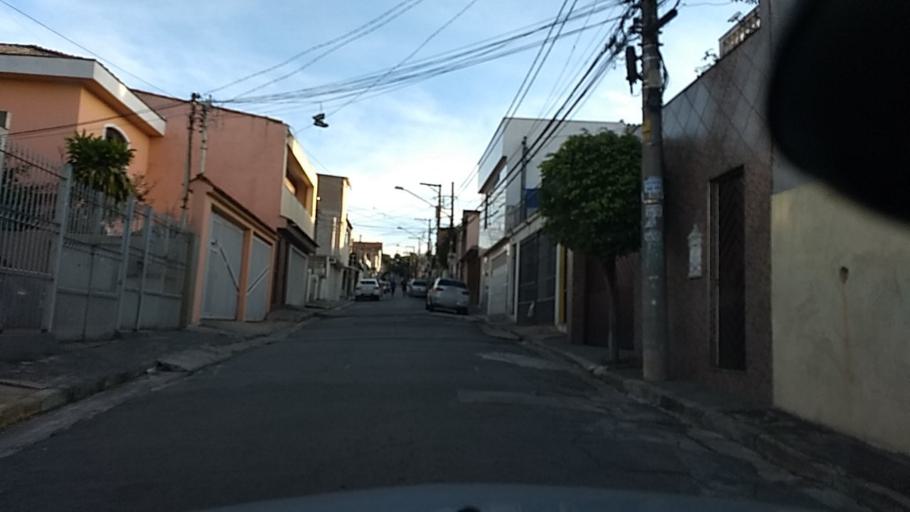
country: BR
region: Sao Paulo
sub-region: Guarulhos
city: Guarulhos
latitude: -23.4943
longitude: -46.5860
